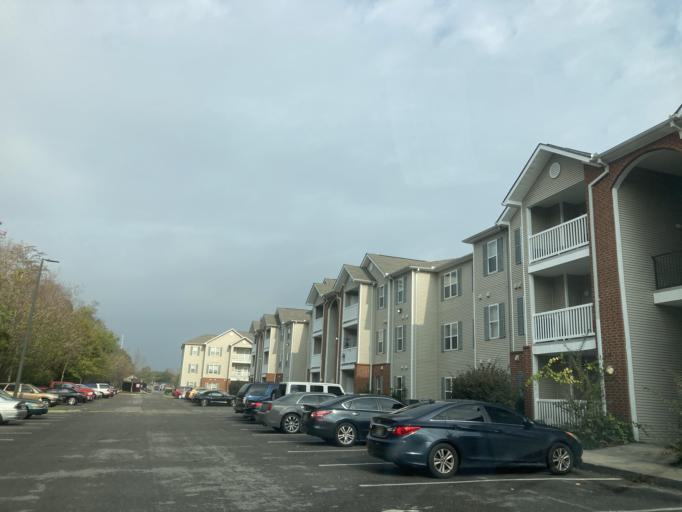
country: US
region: Mississippi
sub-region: Harrison County
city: Gulfport
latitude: 30.3686
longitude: -89.1207
